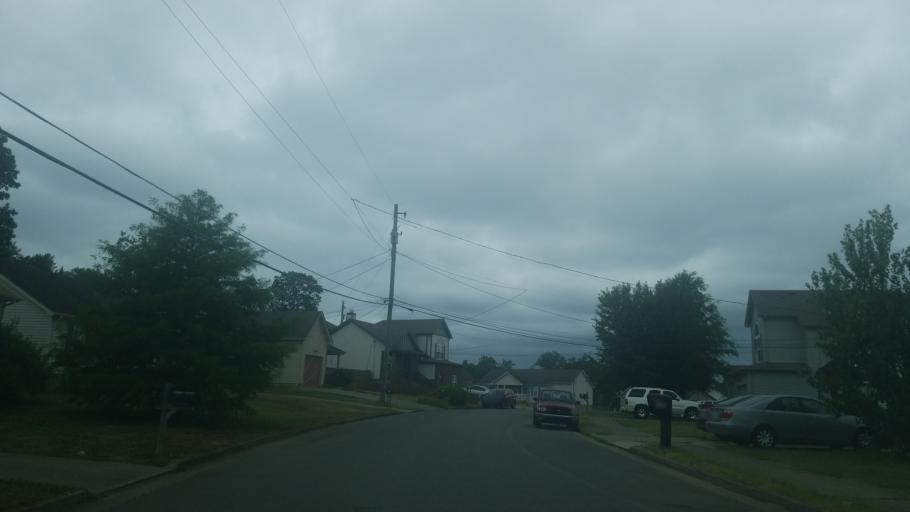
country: US
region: Tennessee
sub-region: Rutherford County
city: La Vergne
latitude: 36.0434
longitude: -86.5933
